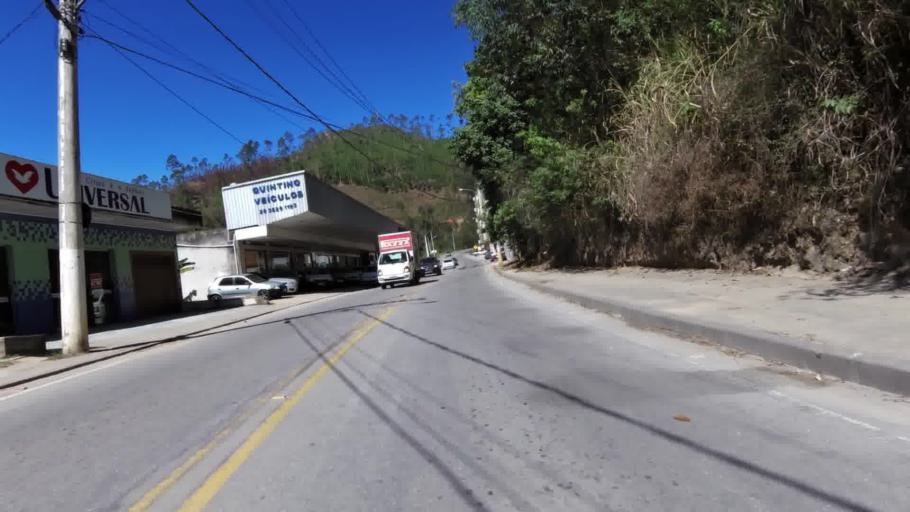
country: BR
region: Espirito Santo
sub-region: Vargem Alta
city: Vargem Alta
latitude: -20.6766
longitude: -41.0129
